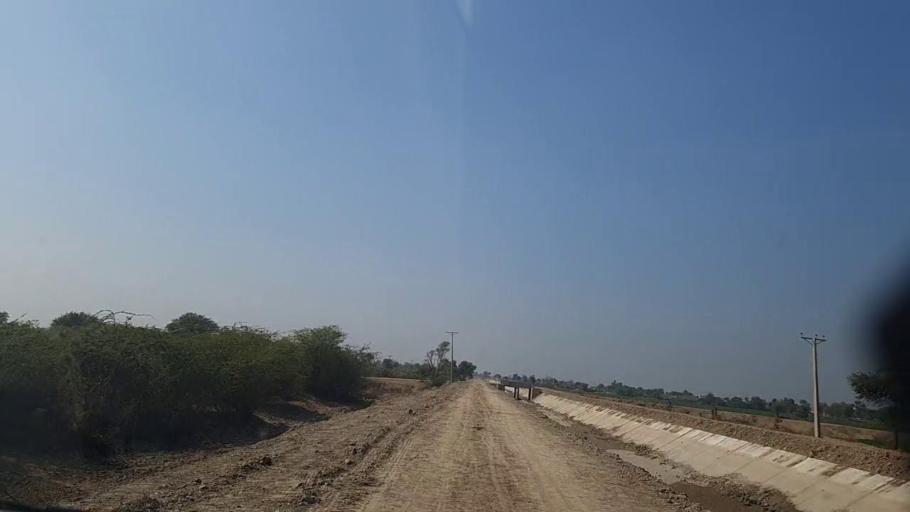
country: PK
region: Sindh
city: Sakrand
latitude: 26.1467
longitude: 68.3477
